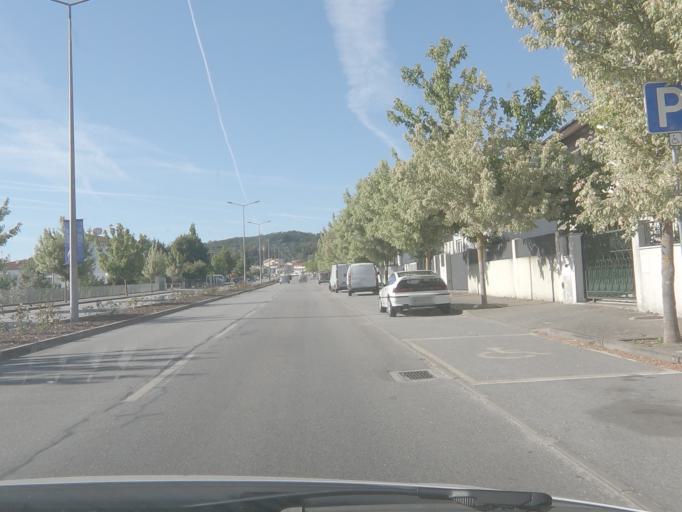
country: PT
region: Viseu
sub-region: Viseu
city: Abraveses
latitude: 40.6866
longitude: -7.9274
